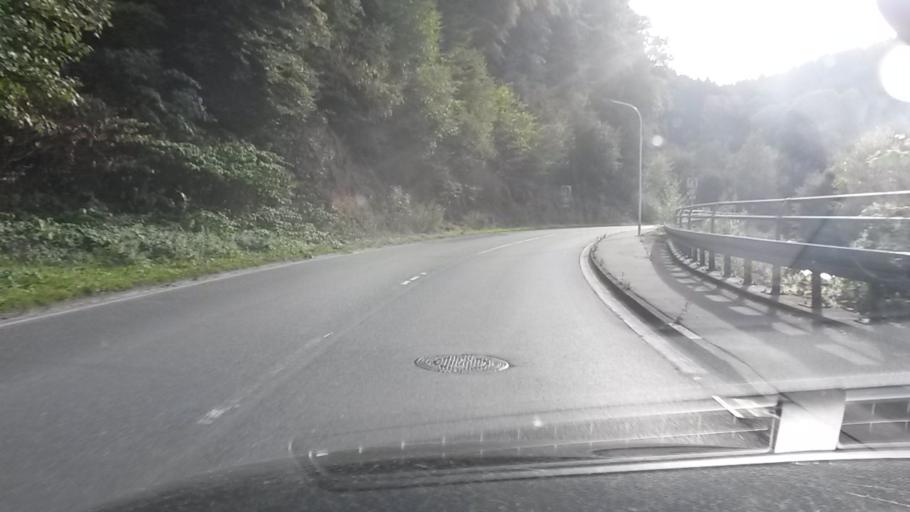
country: DE
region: North Rhine-Westphalia
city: Werdohl
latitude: 51.2311
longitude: 7.7236
